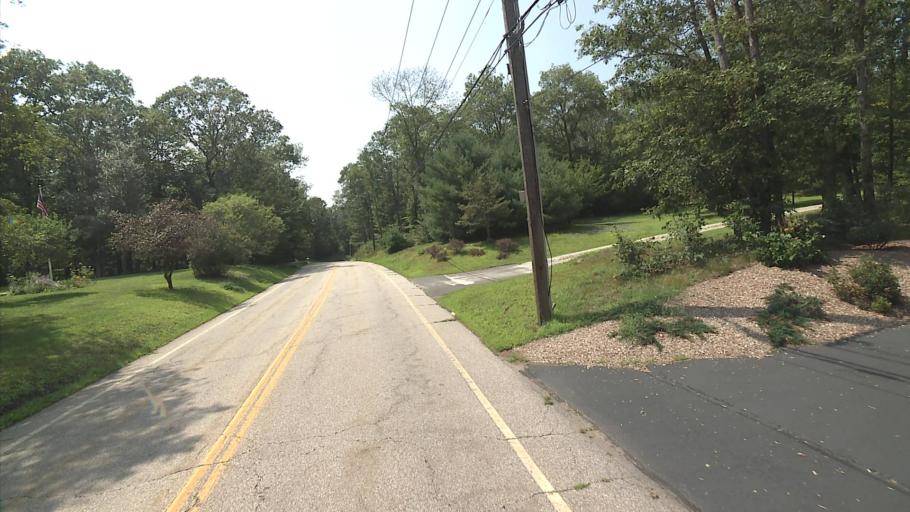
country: US
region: Connecticut
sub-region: Middlesex County
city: Essex Village
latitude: 41.4231
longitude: -72.3843
